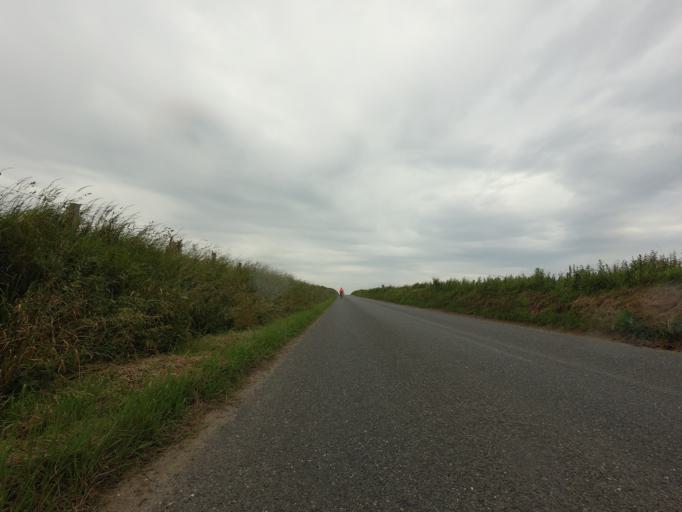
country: GB
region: Scotland
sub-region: Aberdeenshire
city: Whitehills
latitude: 57.6704
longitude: -2.6138
